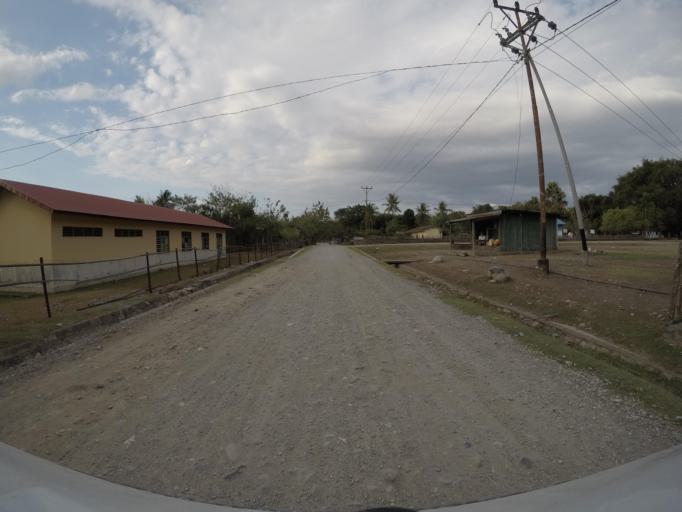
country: TL
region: Bobonaro
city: Maliana
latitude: -8.8804
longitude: 125.2111
